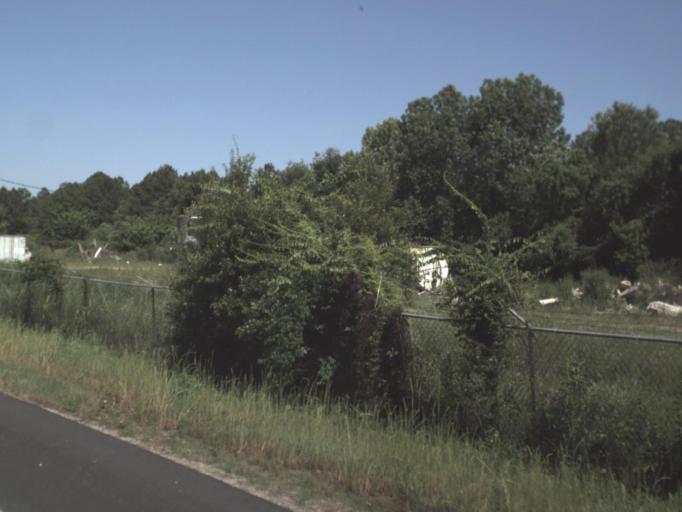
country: US
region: Florida
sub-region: Duval County
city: Jacksonville
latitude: 30.3205
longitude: -81.7919
